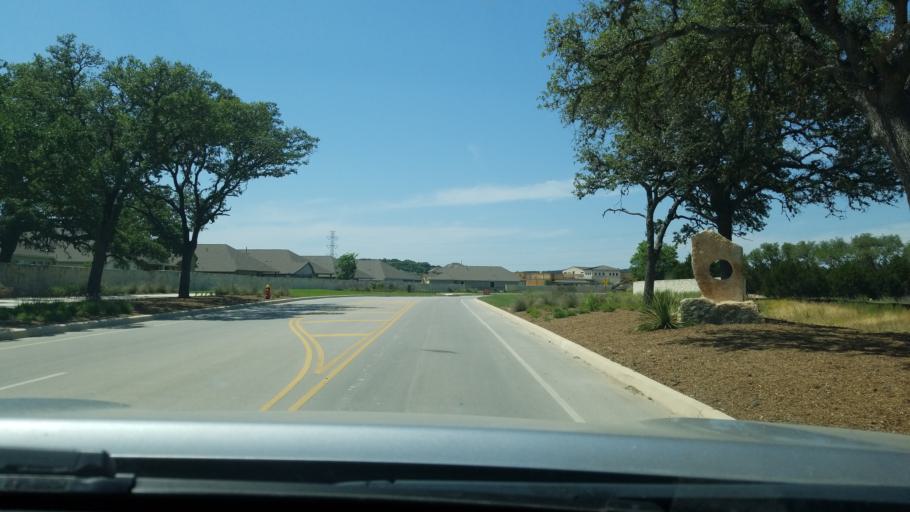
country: US
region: Texas
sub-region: Kendall County
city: Boerne
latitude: 29.8022
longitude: -98.6927
